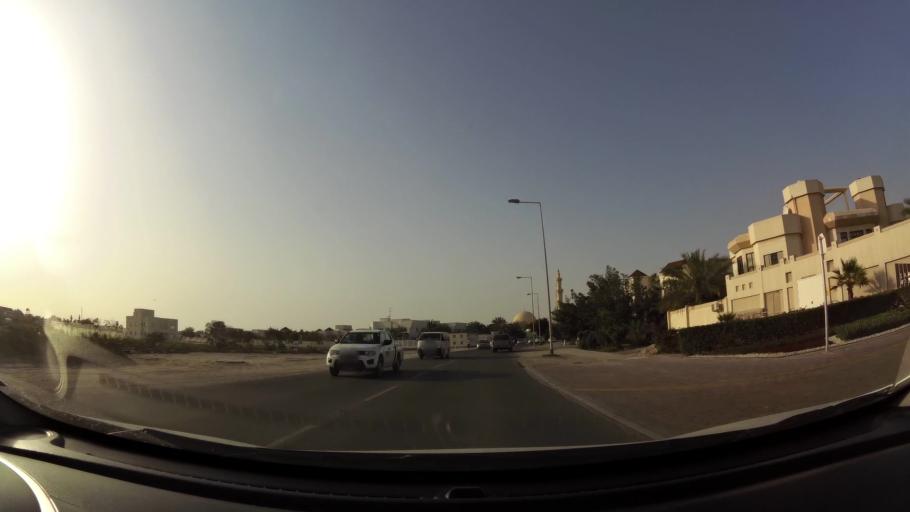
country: BH
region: Manama
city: Jidd Hafs
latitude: 26.2103
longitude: 50.4811
